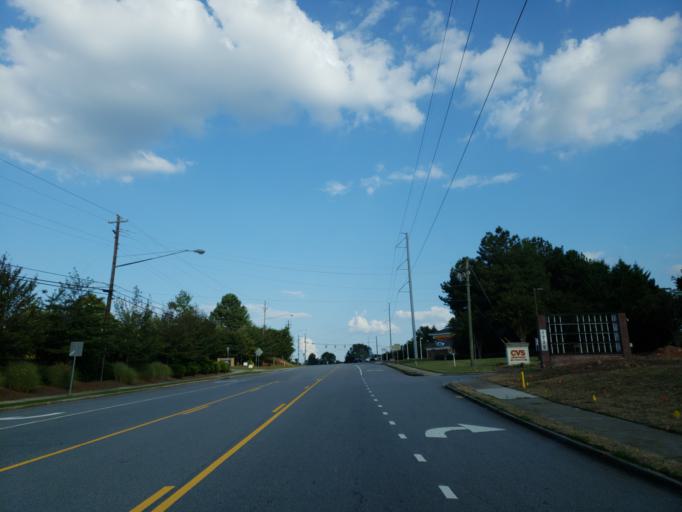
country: US
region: Georgia
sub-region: Fulton County
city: Alpharetta
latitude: 34.0670
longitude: -84.3215
